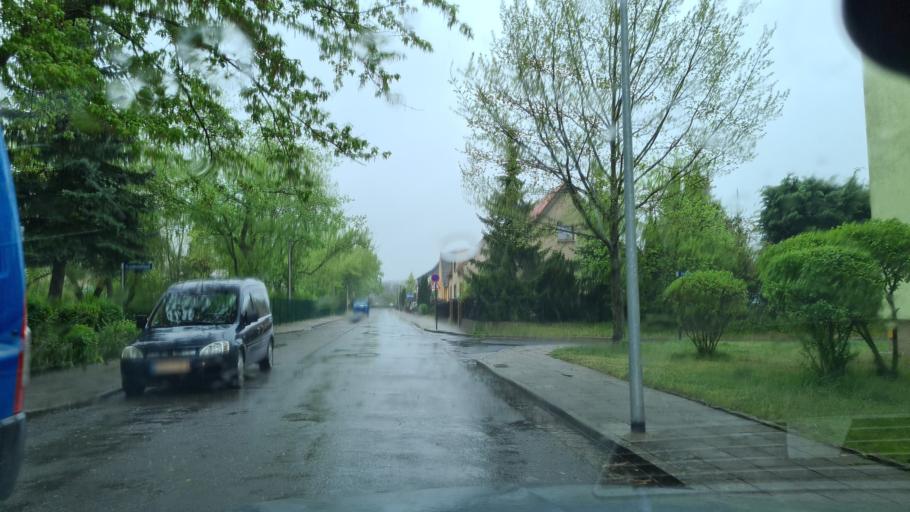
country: DE
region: Brandenburg
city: Elsterwerda
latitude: 51.4612
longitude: 13.5067
